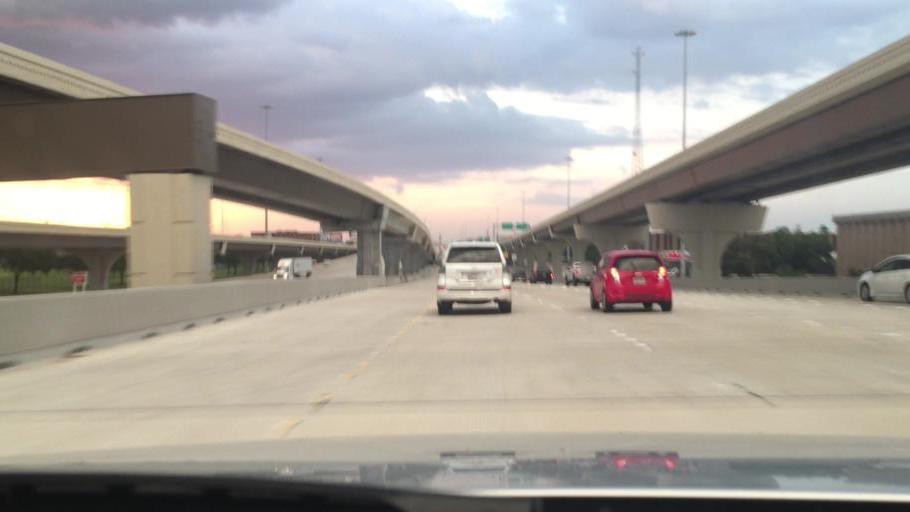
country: US
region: Texas
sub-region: Harris County
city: Spring Valley
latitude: 29.8045
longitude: -95.4515
